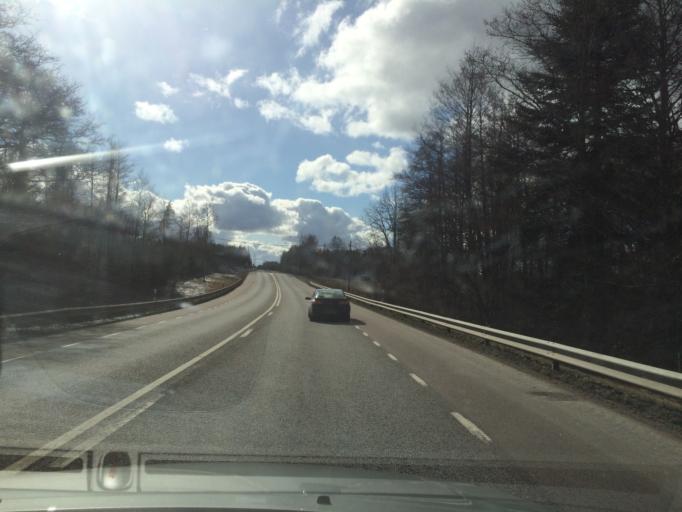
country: SE
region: Vaestra Goetaland
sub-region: Gotene Kommun
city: Goetene
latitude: 58.5937
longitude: 13.6298
